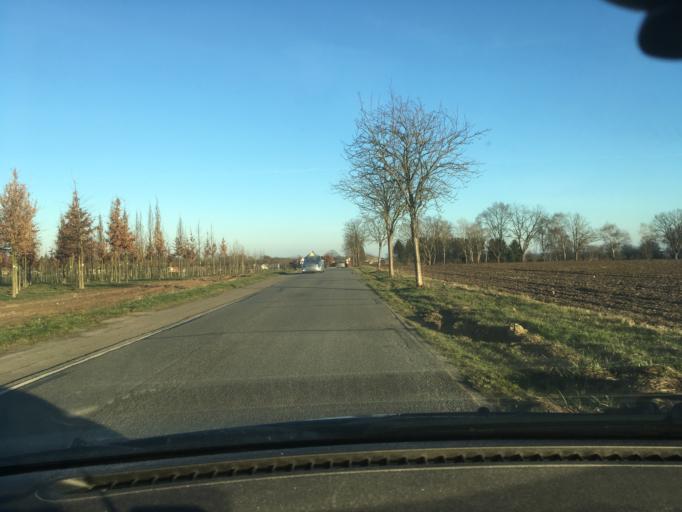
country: DE
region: Lower Saxony
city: Seevetal
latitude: 53.4032
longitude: 9.9595
